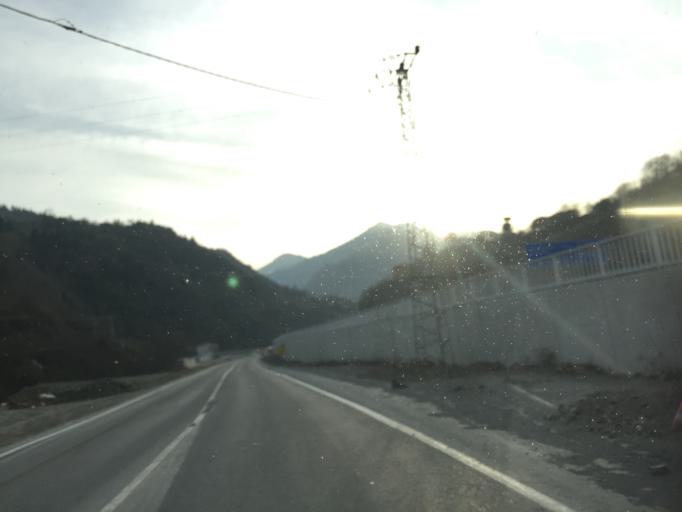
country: TR
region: Trabzon
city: Macka
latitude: 40.8075
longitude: 39.5990
